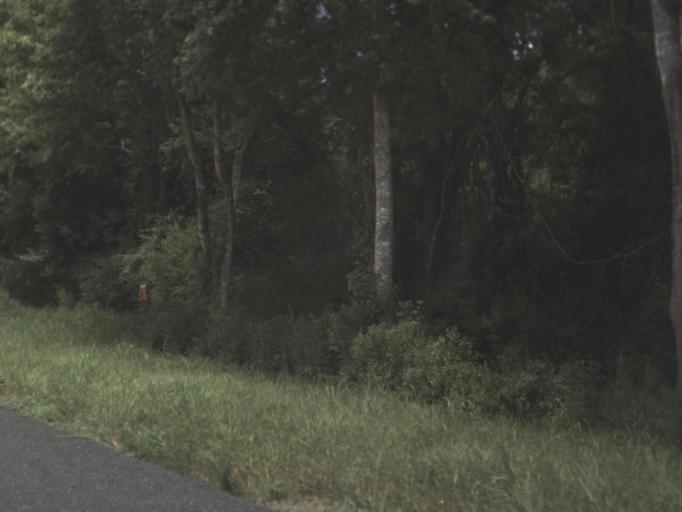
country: US
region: Florida
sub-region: Taylor County
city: Perry
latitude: 30.2164
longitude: -83.6693
